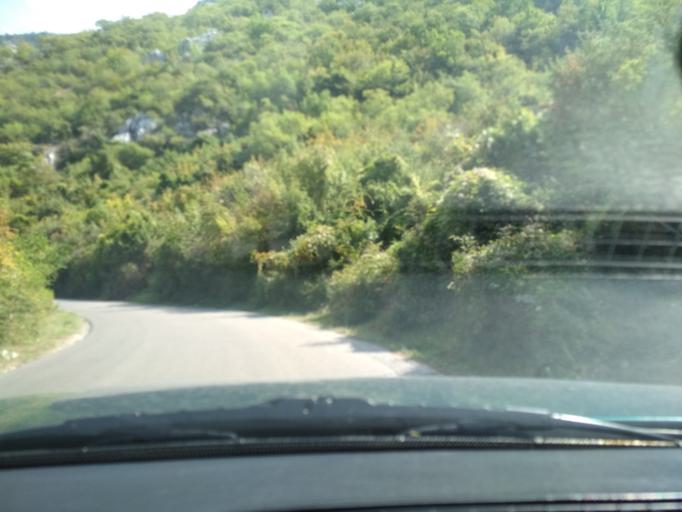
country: ME
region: Kotor
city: Kotor
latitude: 42.3992
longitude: 18.7714
